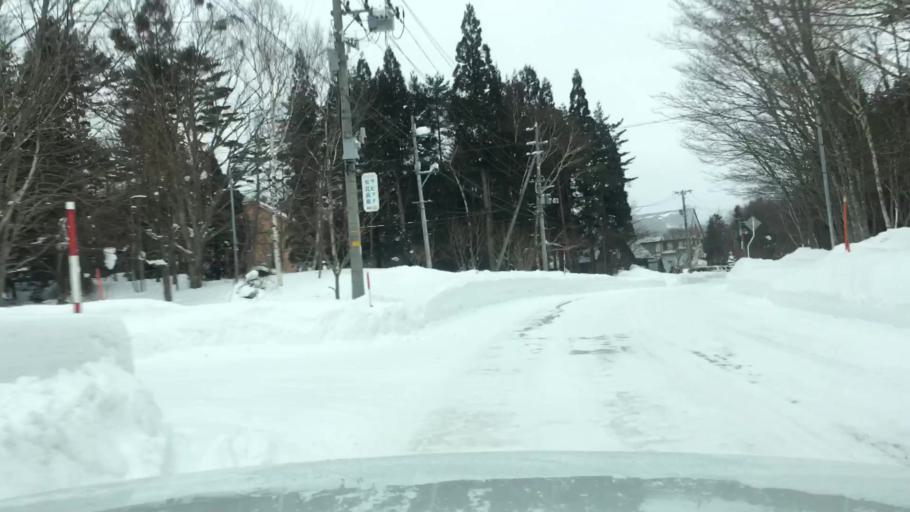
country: JP
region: Akita
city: Hanawa
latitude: 40.0031
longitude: 140.9818
